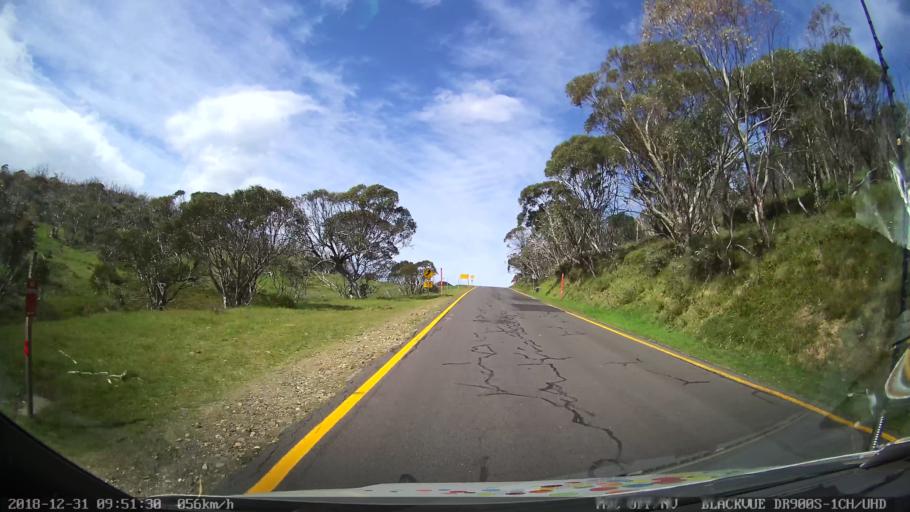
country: AU
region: New South Wales
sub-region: Snowy River
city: Jindabyne
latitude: -36.5233
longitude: 148.2615
